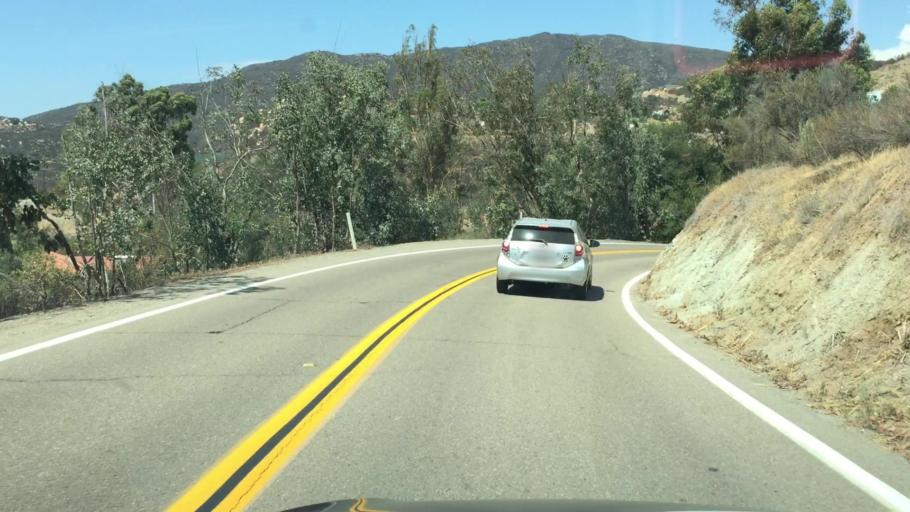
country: US
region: California
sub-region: San Diego County
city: Jamul
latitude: 32.7355
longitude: -116.8163
